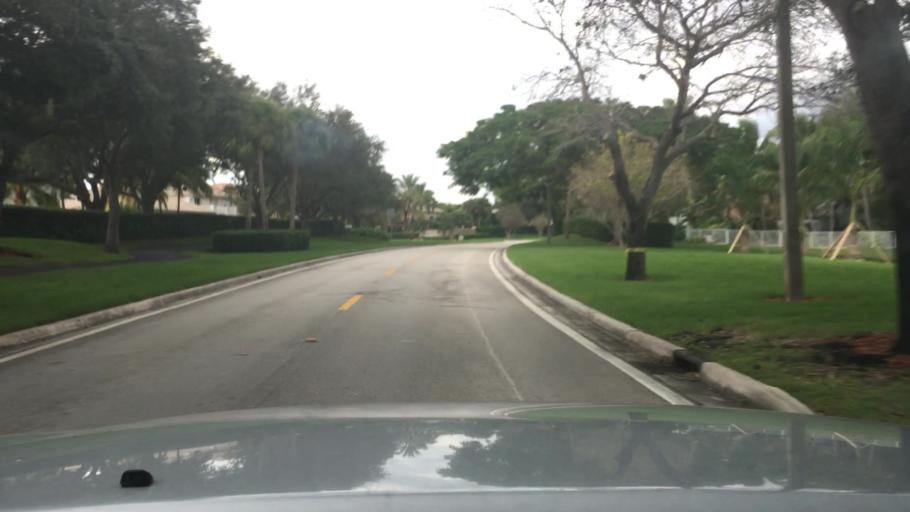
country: US
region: Florida
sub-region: Broward County
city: Sunshine Ranches
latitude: 26.0028
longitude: -80.3684
